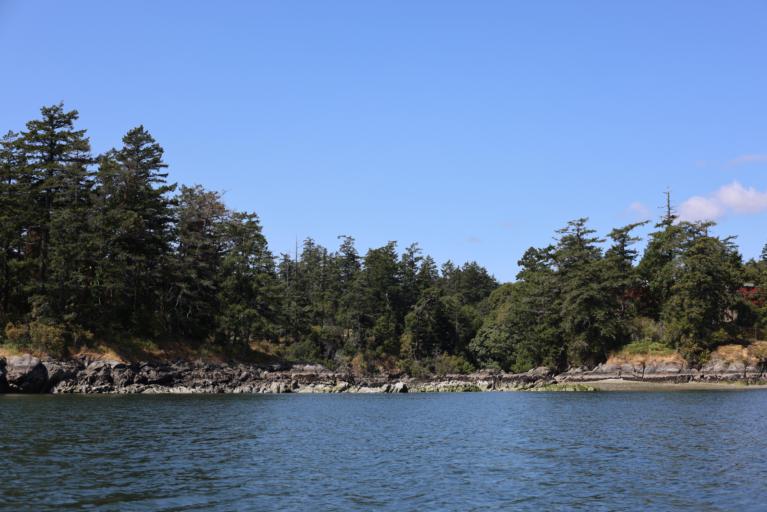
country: CA
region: British Columbia
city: Colwood
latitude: 48.4488
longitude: -123.4476
